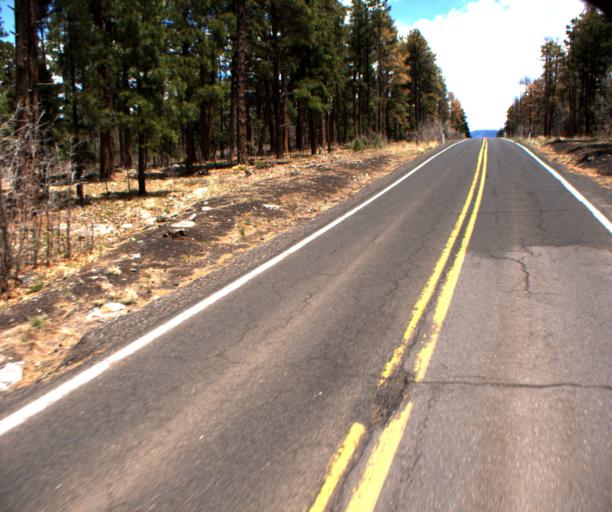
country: US
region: Arizona
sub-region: Coconino County
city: Kachina Village
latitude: 35.1115
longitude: -111.7151
